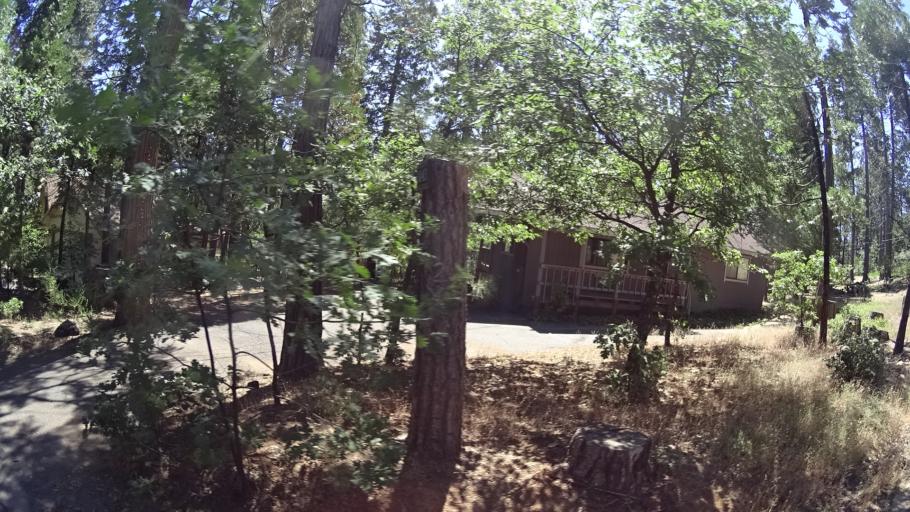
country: US
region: California
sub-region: Calaveras County
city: Arnold
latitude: 38.2304
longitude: -120.3739
